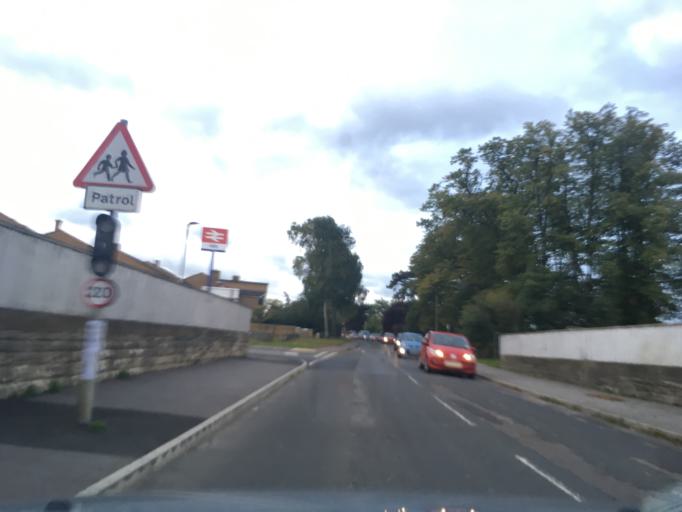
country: GB
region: England
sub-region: Oxfordshire
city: Kidlington
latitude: 51.8252
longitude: -1.2393
